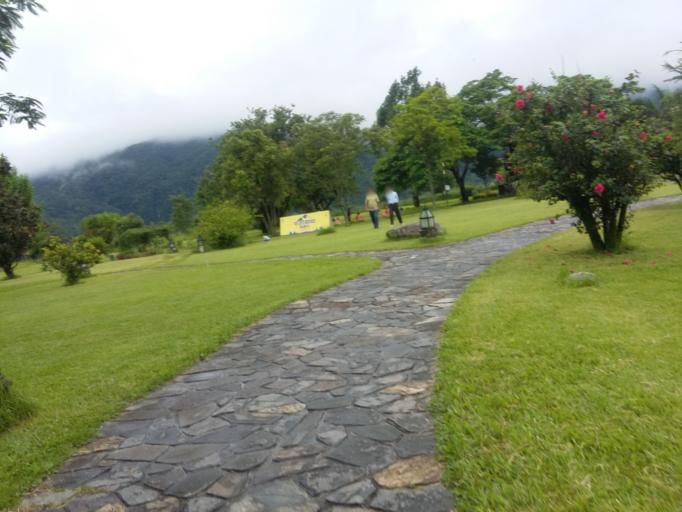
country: NP
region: Western Region
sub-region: Gandaki Zone
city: Pokhara
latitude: 28.1766
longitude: 83.9993
